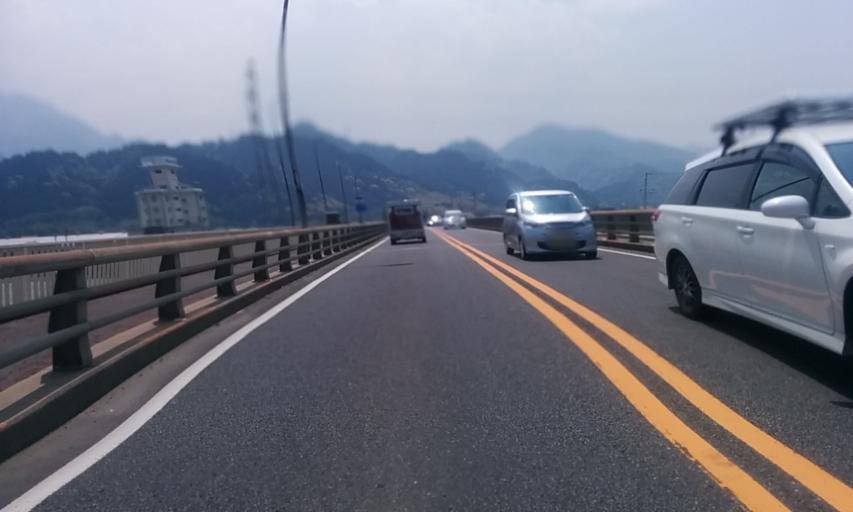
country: JP
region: Ehime
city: Saijo
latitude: 33.9037
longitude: 133.1845
